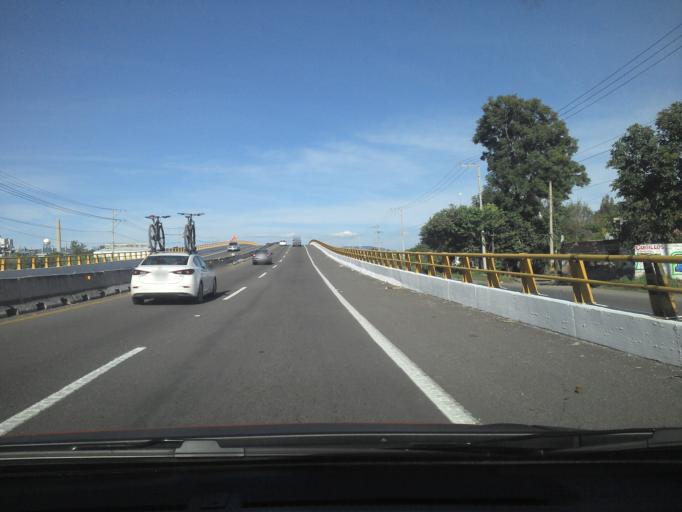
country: MX
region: Jalisco
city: El Refugio
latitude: 20.6636
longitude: -103.7242
